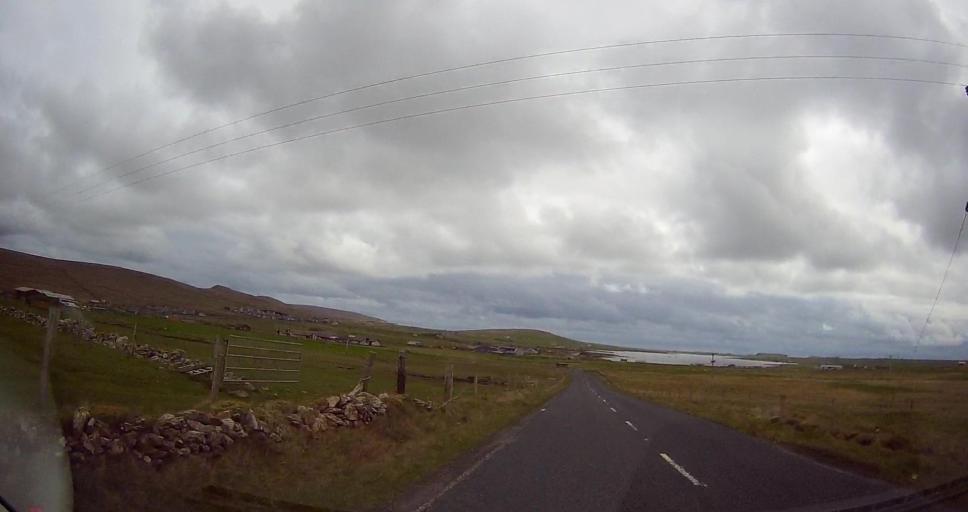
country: GB
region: Scotland
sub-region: Shetland Islands
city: Shetland
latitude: 60.7550
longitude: -0.8830
